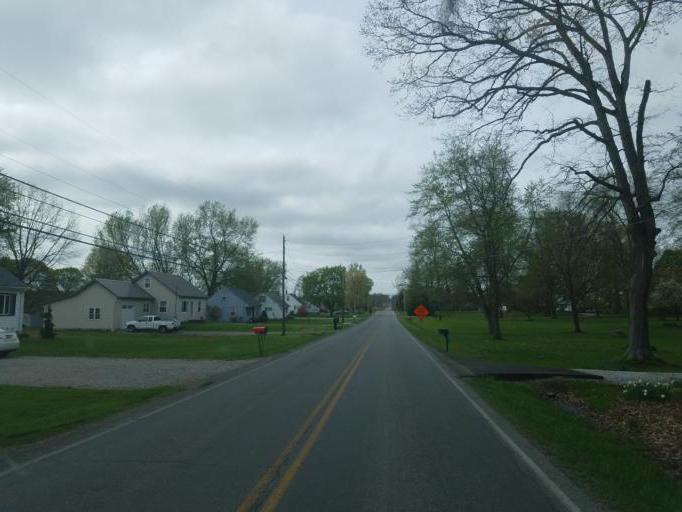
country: US
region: Ohio
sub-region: Wayne County
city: Apple Creek
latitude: 40.7601
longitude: -81.8959
